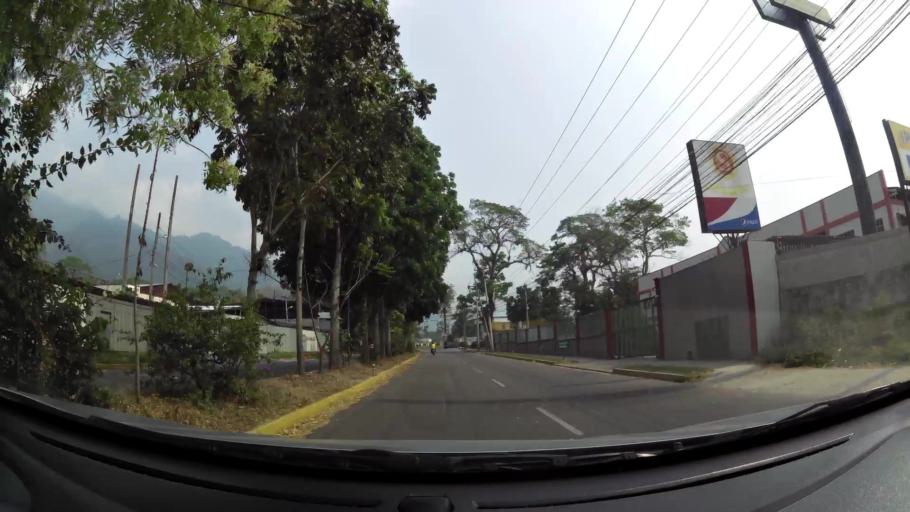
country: HN
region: Cortes
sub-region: San Pedro Sula
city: Pena Blanca
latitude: 15.5441
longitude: -88.0332
